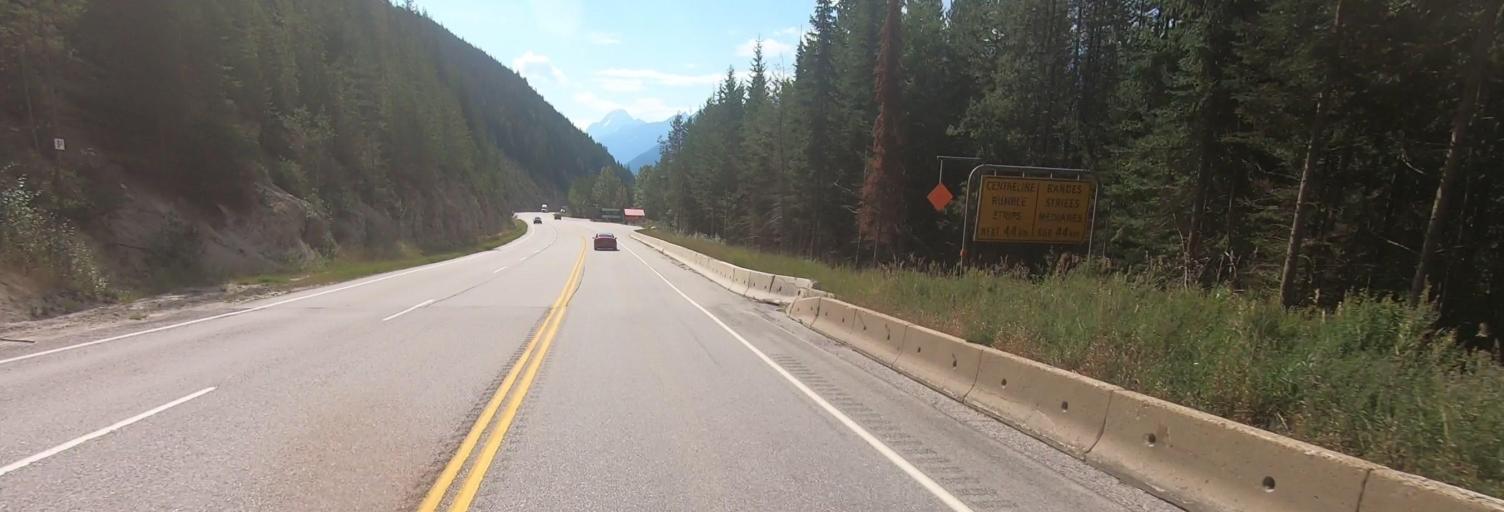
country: CA
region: British Columbia
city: Golden
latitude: 51.4648
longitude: -117.4805
